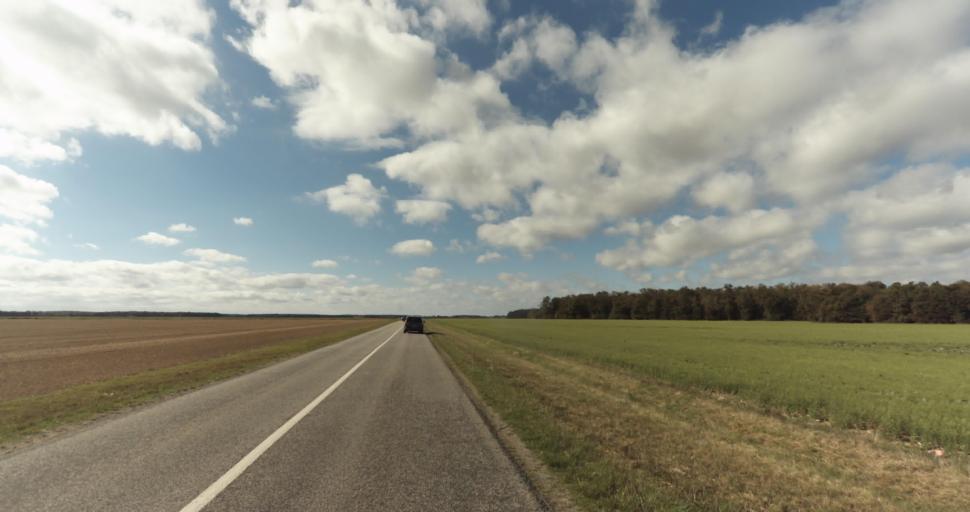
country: FR
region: Centre
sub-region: Departement d'Eure-et-Loir
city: Garnay
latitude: 48.7195
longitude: 1.3209
